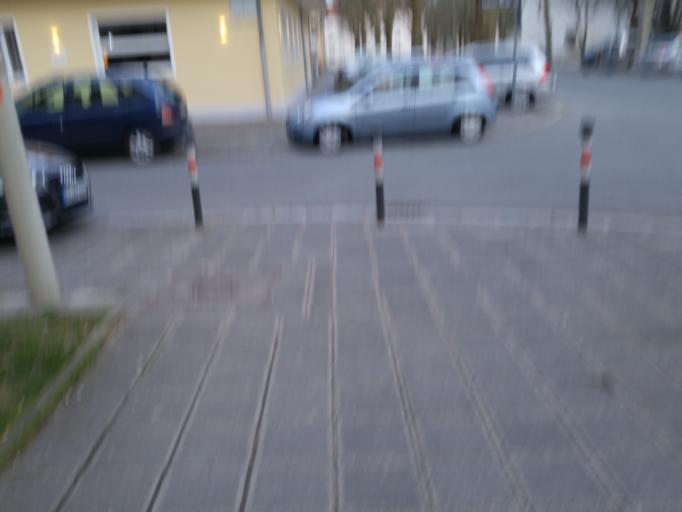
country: DE
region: Bavaria
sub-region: Regierungsbezirk Mittelfranken
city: Nuernberg
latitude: 49.4712
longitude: 11.1097
